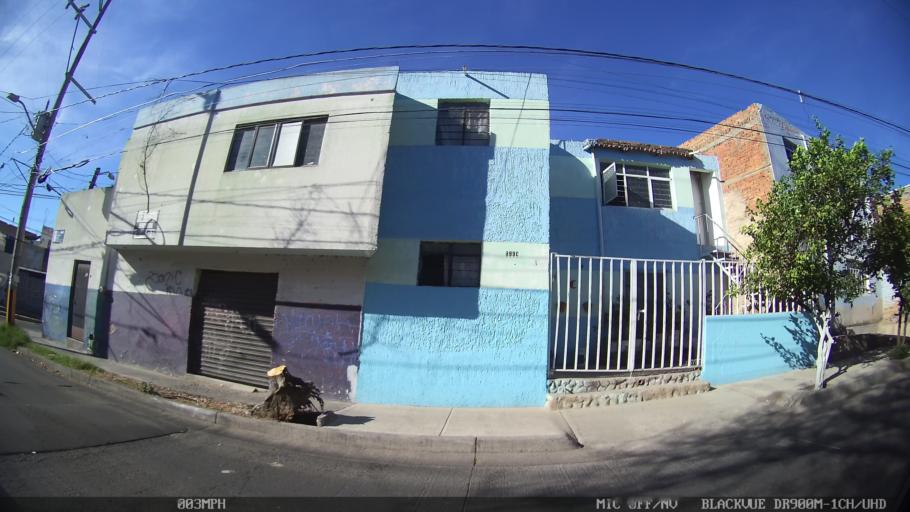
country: MX
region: Jalisco
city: Tlaquepaque
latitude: 20.6784
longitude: -103.2720
